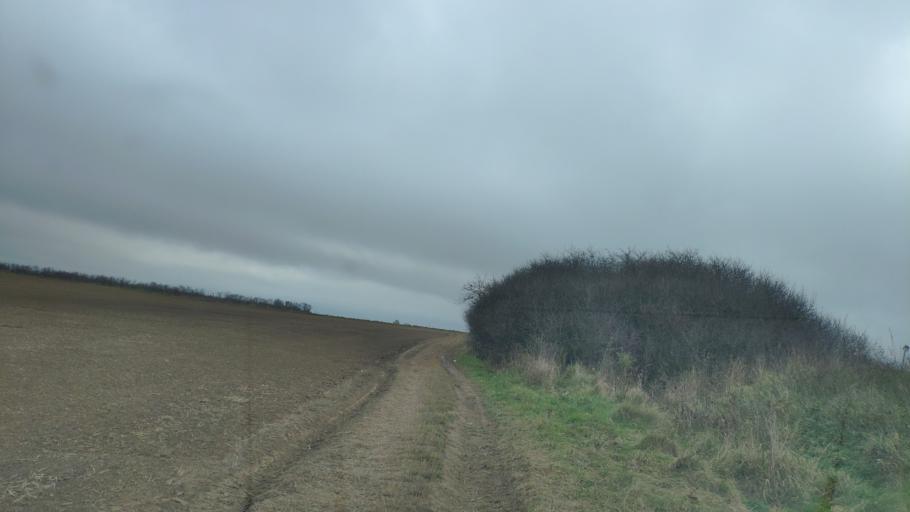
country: SK
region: Presovsky
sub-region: Okres Presov
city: Presov
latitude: 49.0143
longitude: 21.2093
